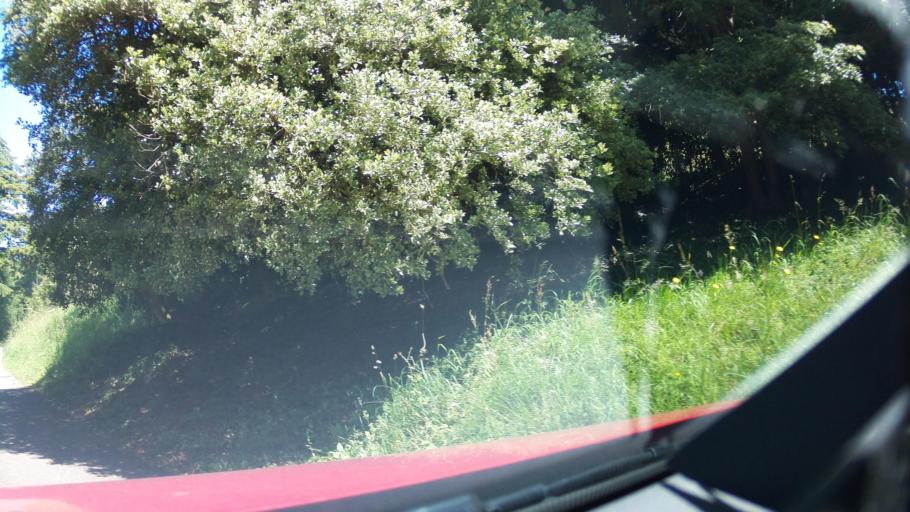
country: GB
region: England
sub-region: Devon
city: Dartmouth
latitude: 50.3836
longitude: -3.5864
